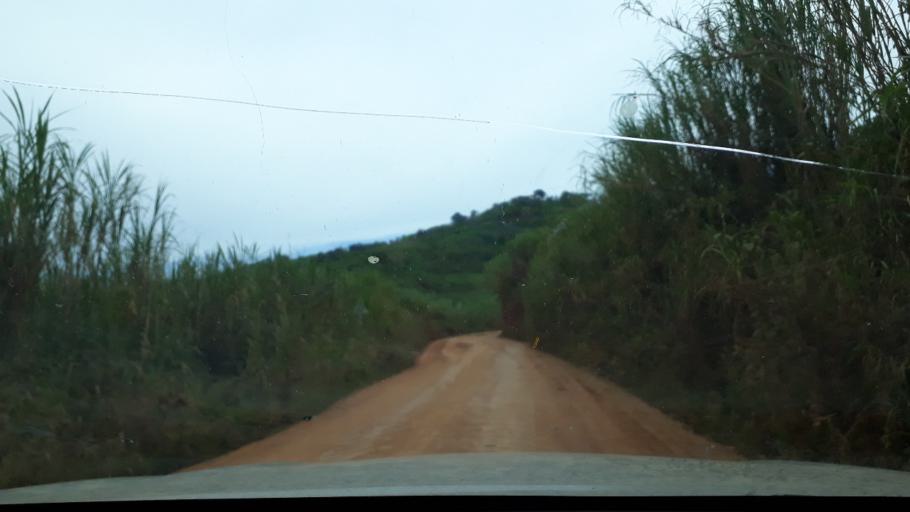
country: CD
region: Eastern Province
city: Bunia
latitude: 1.8095
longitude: 30.4150
